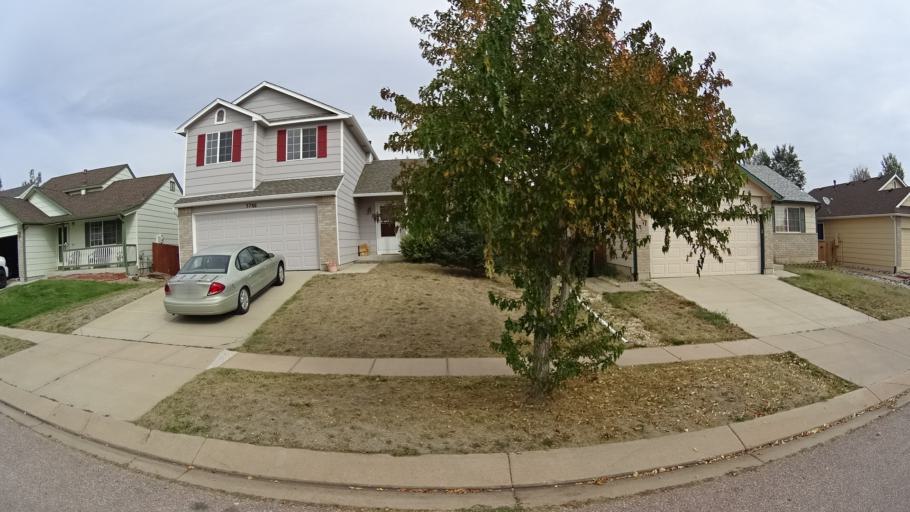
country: US
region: Colorado
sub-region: El Paso County
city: Cimarron Hills
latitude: 38.9173
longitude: -104.7120
